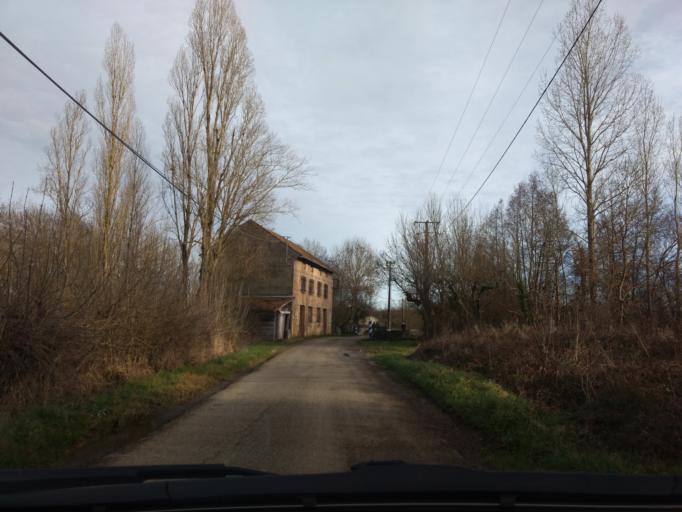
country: FR
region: Midi-Pyrenees
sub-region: Departement du Gers
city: Aubiet
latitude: 43.6735
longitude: 0.7996
